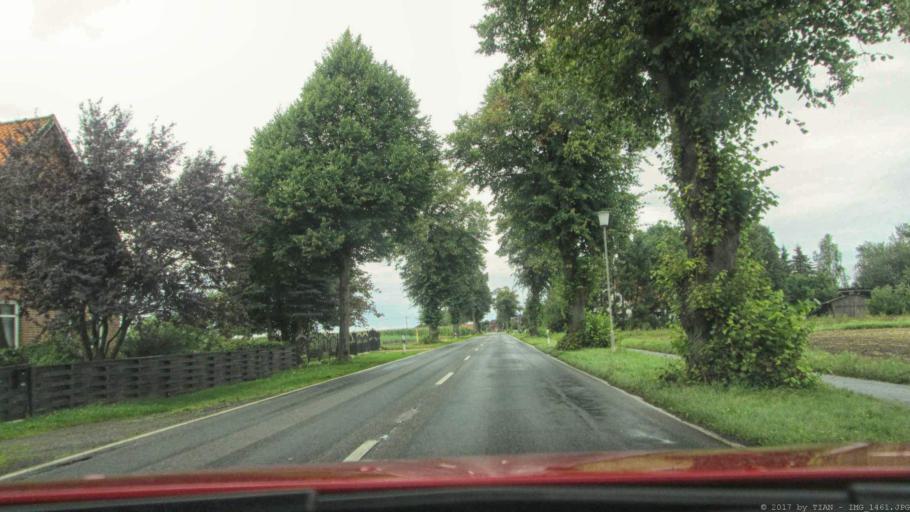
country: DE
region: Lower Saxony
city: Bodenteich
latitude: 52.8037
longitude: 10.7056
